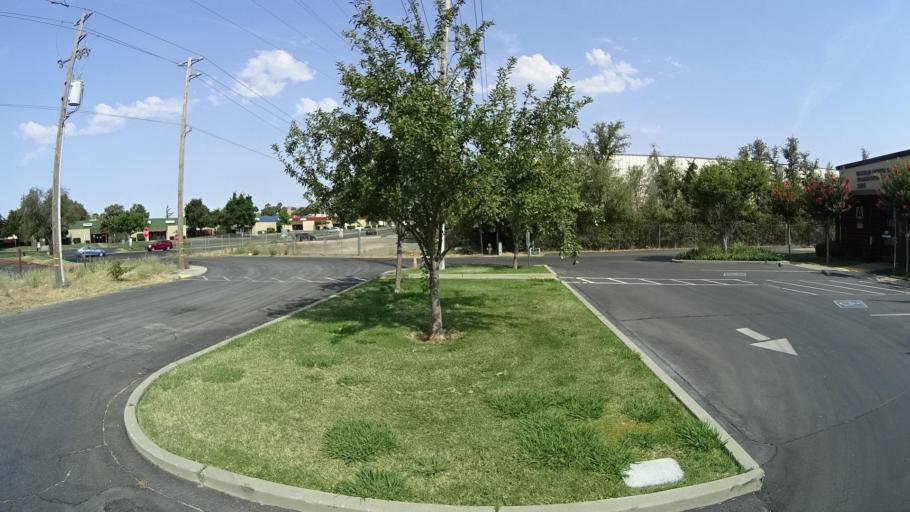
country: US
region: California
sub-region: Placer County
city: Rocklin
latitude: 38.7992
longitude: -121.2221
